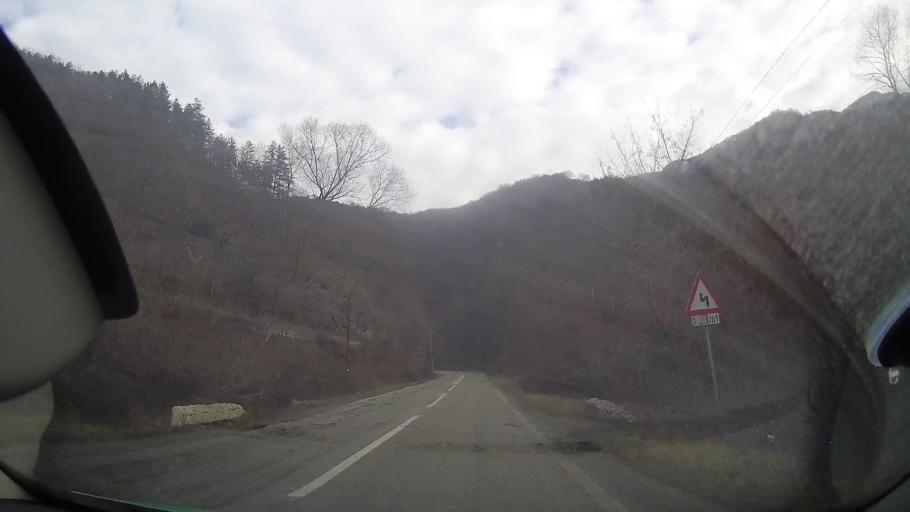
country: RO
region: Alba
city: Salciua de Sus
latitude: 46.4271
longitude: 23.4601
